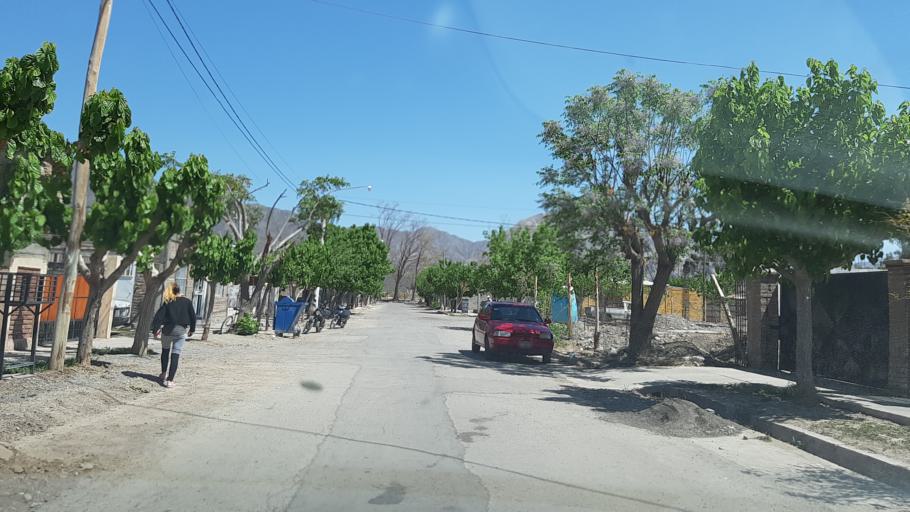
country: AR
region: San Juan
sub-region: Departamento de Zonda
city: Zonda
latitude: -31.5395
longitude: -68.7506
